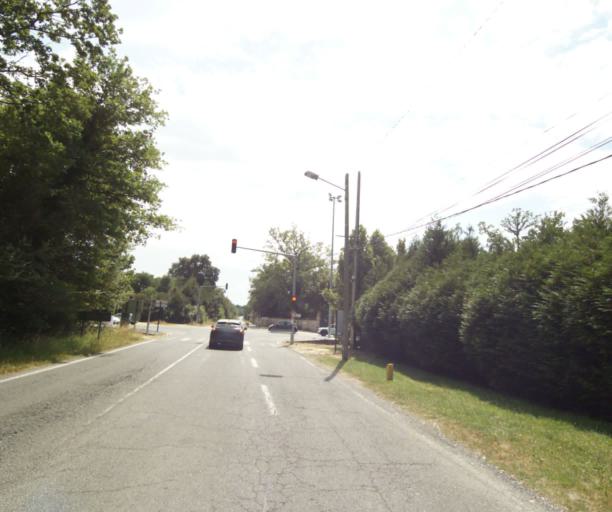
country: FR
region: Ile-de-France
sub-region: Departement de Seine-et-Marne
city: Dammarie-les-Lys
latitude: 48.4975
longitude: 2.6342
